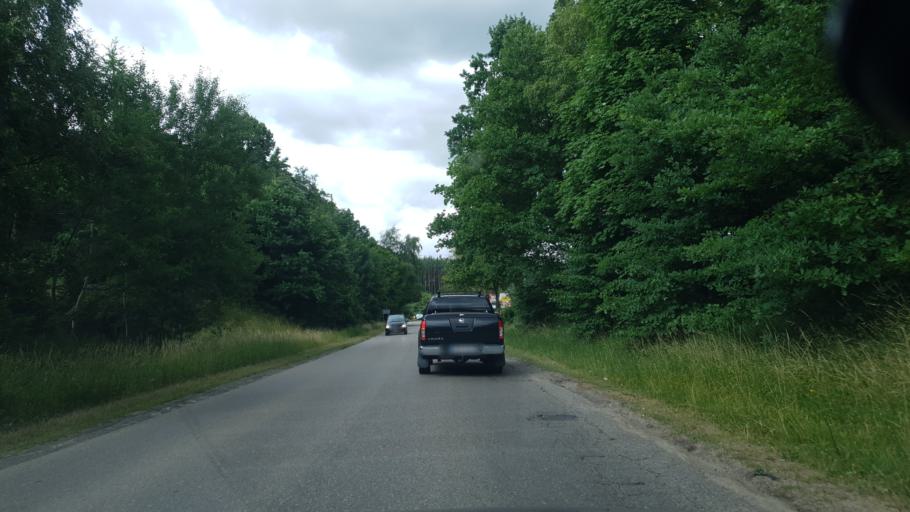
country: PL
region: Pomeranian Voivodeship
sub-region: Powiat kartuski
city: Przodkowo
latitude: 54.3649
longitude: 18.2654
